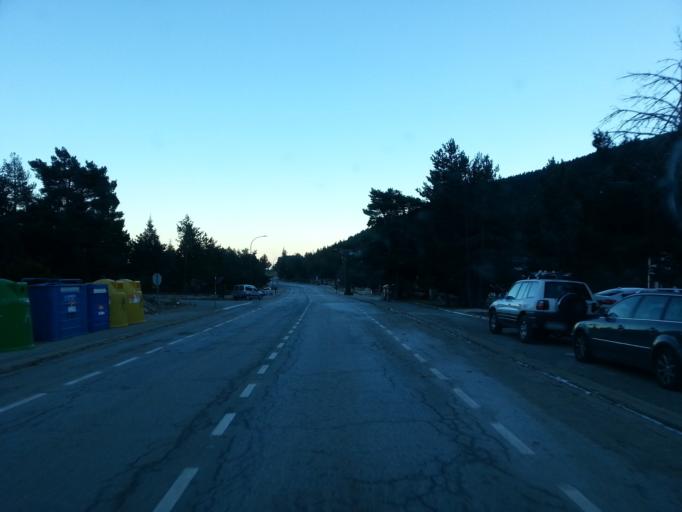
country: ES
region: Catalonia
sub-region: Provincia de Lleida
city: Gosol
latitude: 42.1712
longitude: 1.5690
